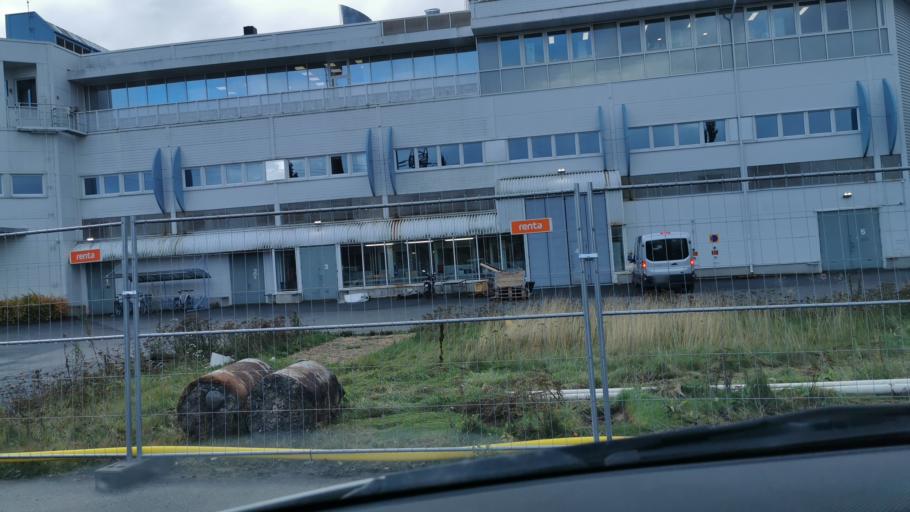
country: FI
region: Ostrobothnia
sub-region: Vaasa
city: Vaasa
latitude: 63.0907
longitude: 21.5573
